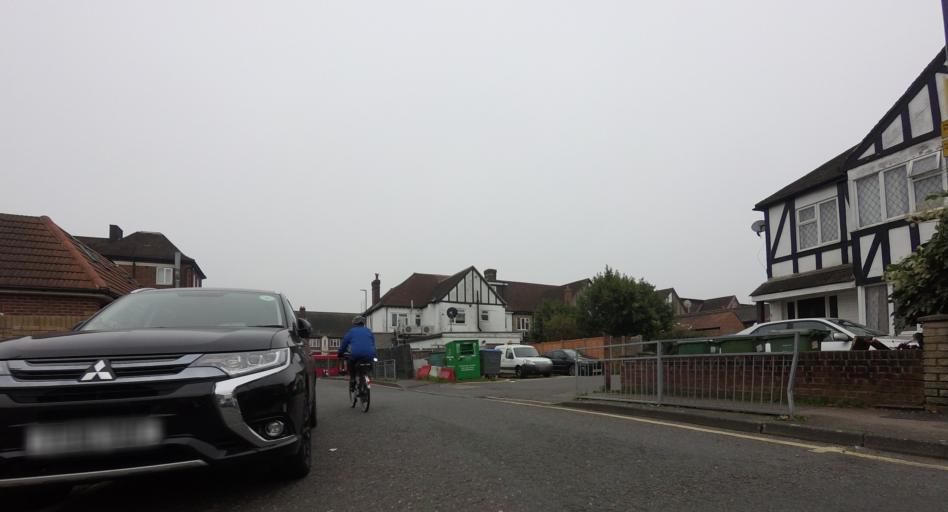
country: GB
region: England
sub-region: Greater London
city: Bexleyheath
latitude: 51.4651
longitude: 0.1321
